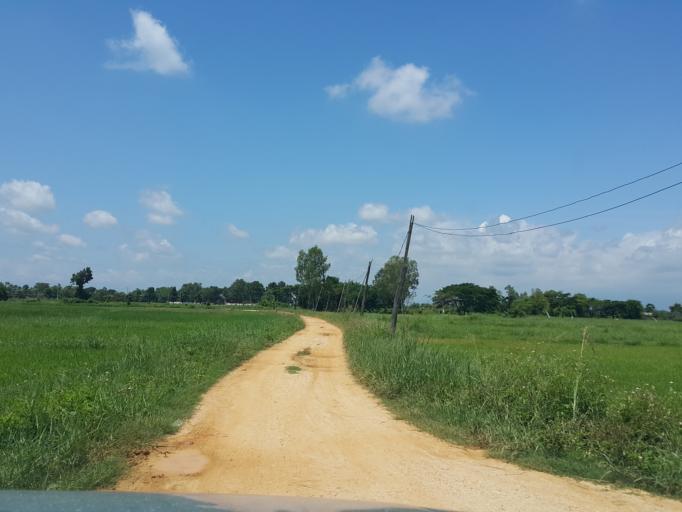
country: TH
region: Lamphun
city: Ban Thi
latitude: 18.6826
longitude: 99.1293
